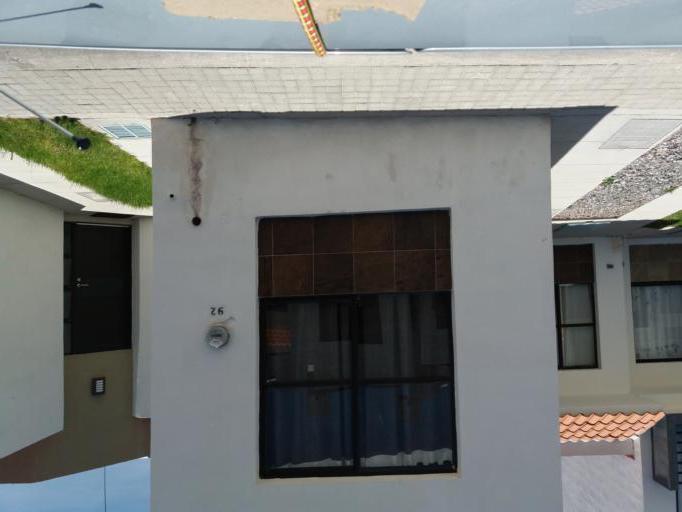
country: MX
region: Aguascalientes
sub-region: Aguascalientes
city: San Sebastian [Fraccionamiento]
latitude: 21.8060
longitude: -102.3025
